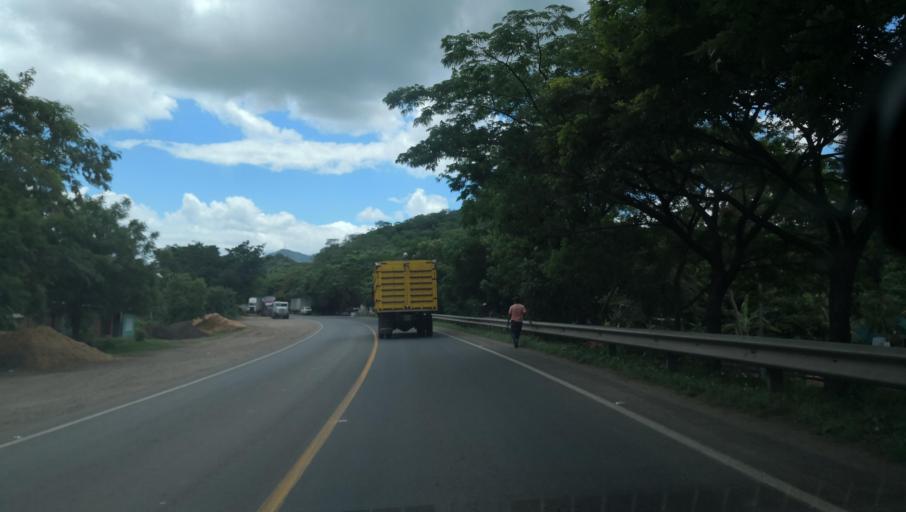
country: NI
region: Madriz
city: Yalaguina
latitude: 13.4731
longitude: -86.4769
